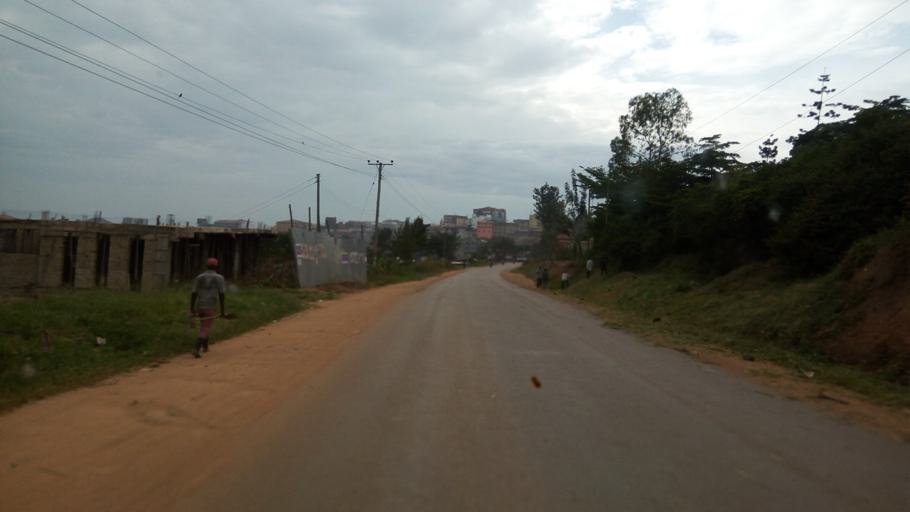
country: UG
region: Western Region
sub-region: Mbarara District
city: Mbarara
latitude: -0.6051
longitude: 30.6551
